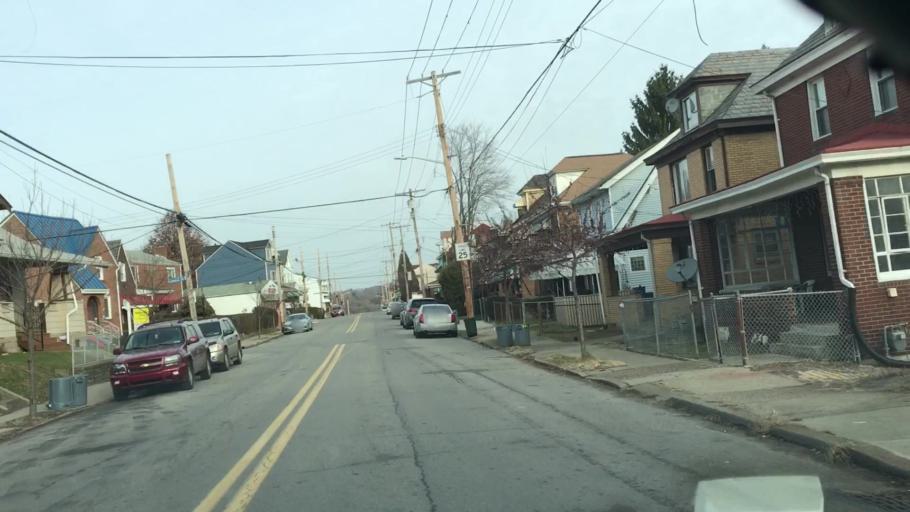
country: US
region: Pennsylvania
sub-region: Allegheny County
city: Bellevue
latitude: 40.4720
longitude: -80.0310
